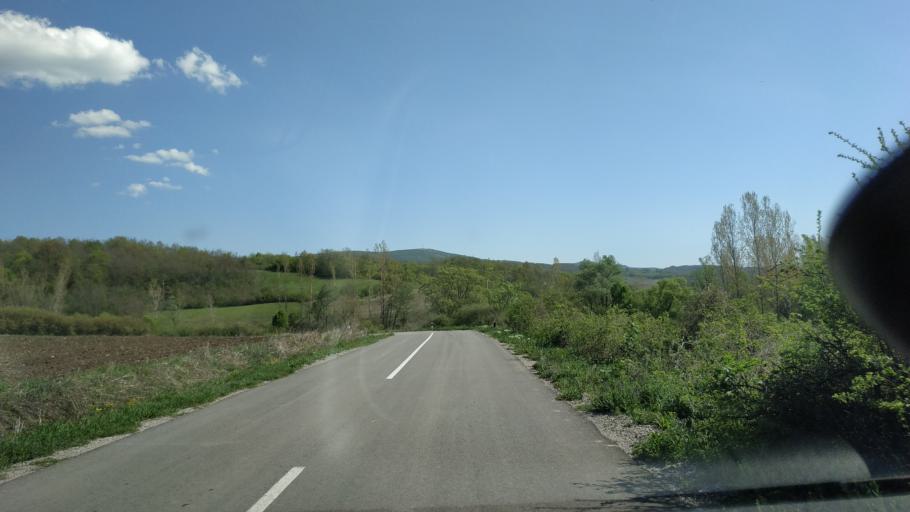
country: RS
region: Central Serbia
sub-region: Zajecarski Okrug
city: Soko Banja
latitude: 43.4828
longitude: 21.8688
